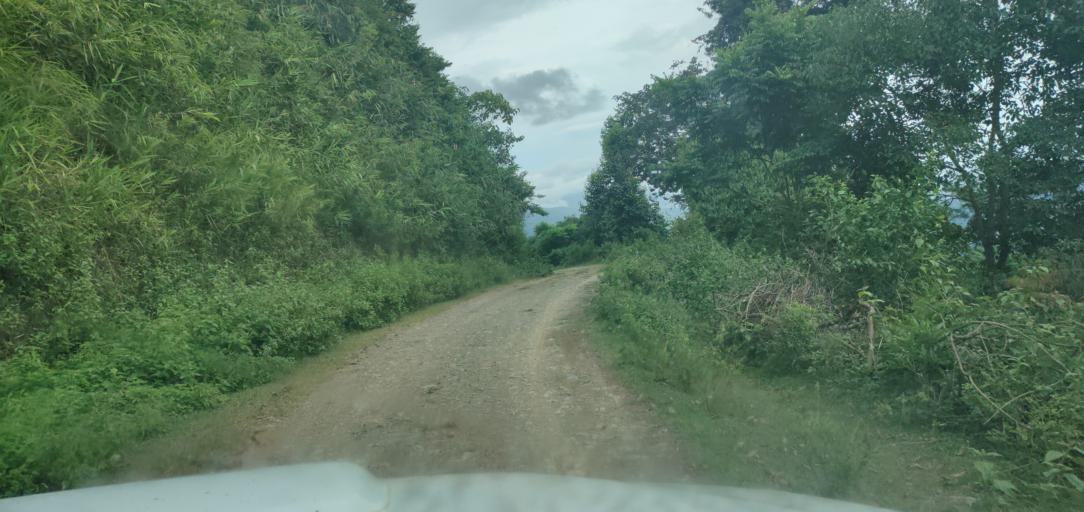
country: LA
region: Phongsali
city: Phongsali
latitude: 21.4475
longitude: 102.3091
